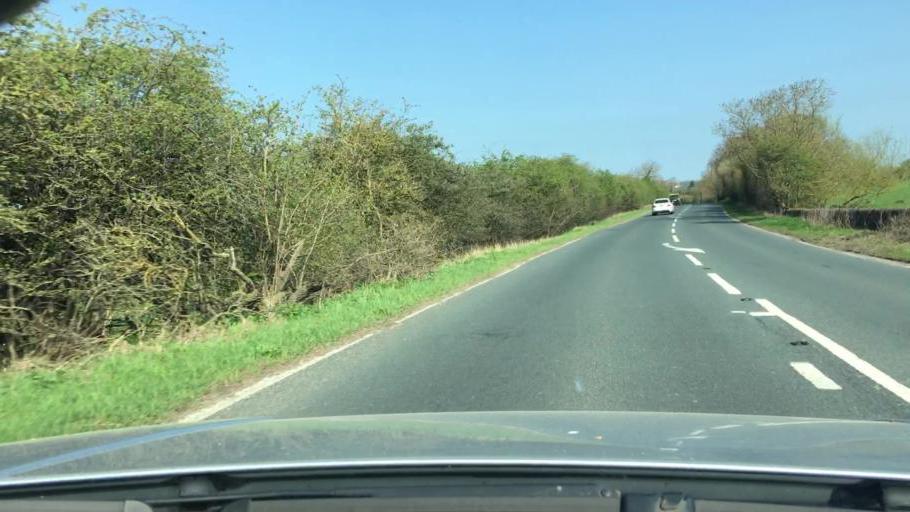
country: GB
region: England
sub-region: North Yorkshire
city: Pannal
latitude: 53.9417
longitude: -1.5378
